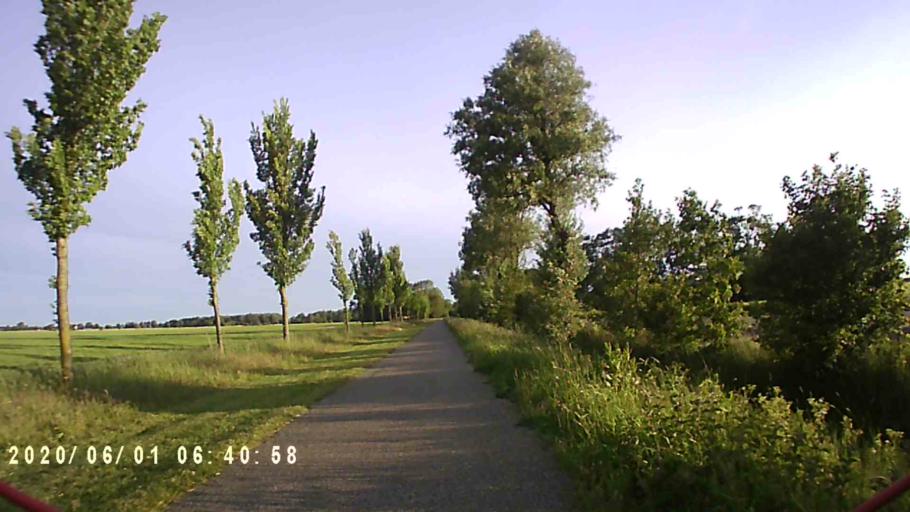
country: NL
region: Friesland
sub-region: Gemeente Kollumerland en Nieuwkruisland
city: Kollum
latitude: 53.2943
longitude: 6.1557
